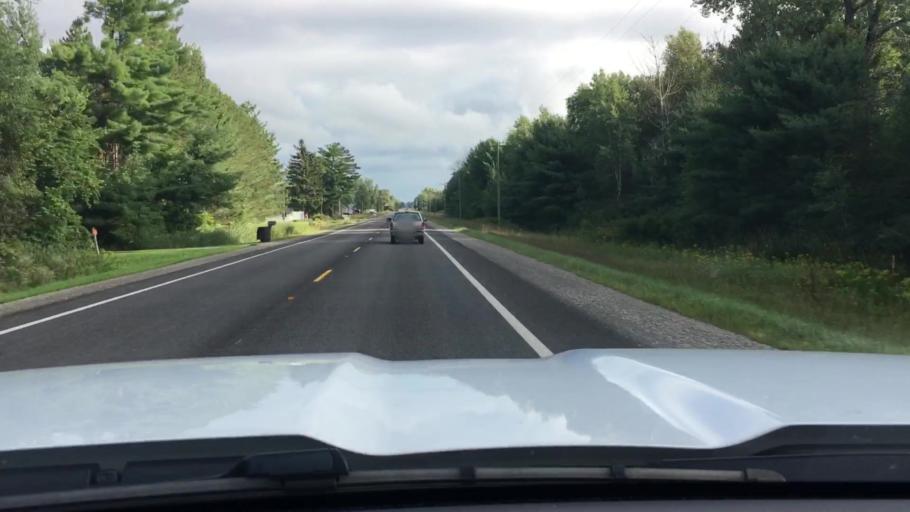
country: US
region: Michigan
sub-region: Tuscola County
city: Caro
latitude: 43.4335
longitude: -83.3849
